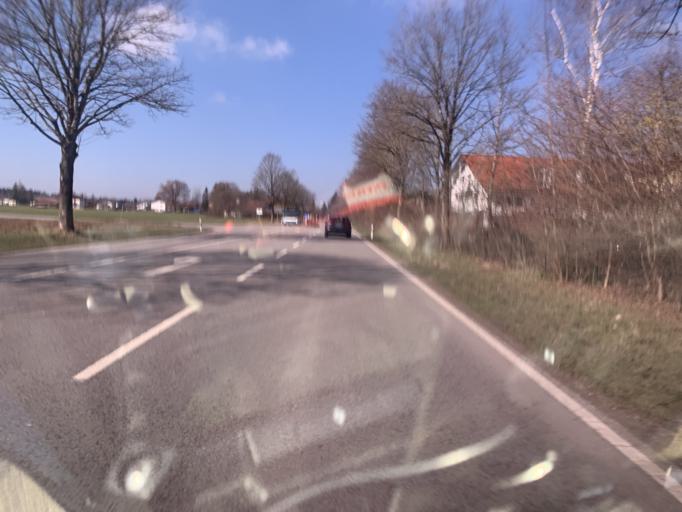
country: DE
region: Bavaria
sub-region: Upper Bavaria
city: Brunnthal
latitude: 47.9837
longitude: 11.7070
